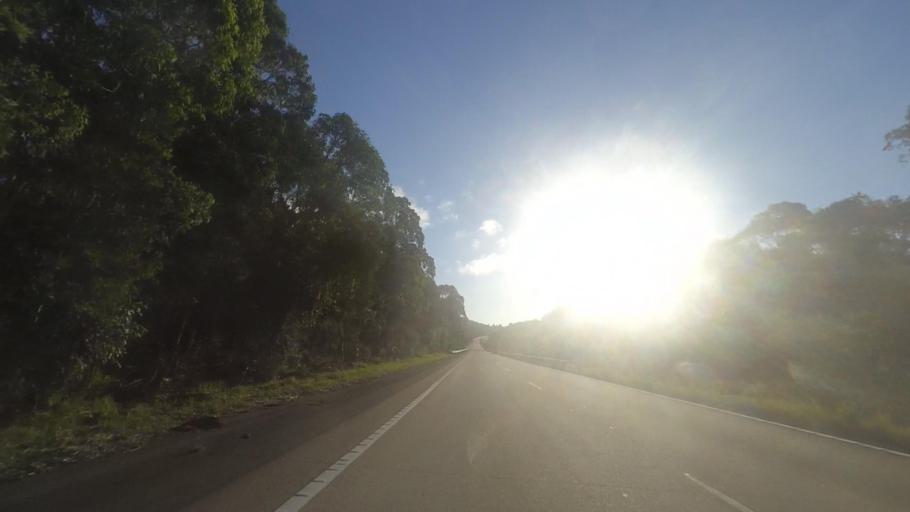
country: AU
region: New South Wales
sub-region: Great Lakes
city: Bulahdelah
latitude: -32.3811
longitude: 152.2679
